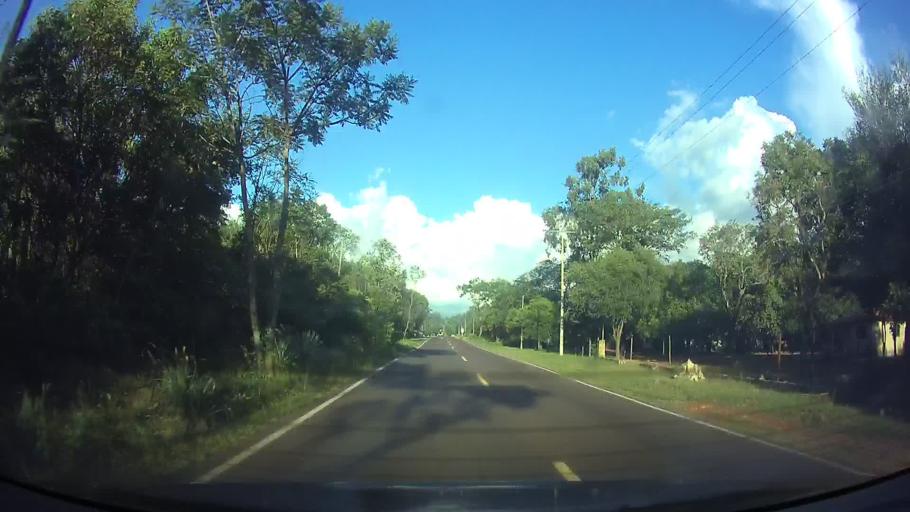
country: PY
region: Cordillera
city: Emboscada
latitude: -25.2036
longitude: -57.3387
